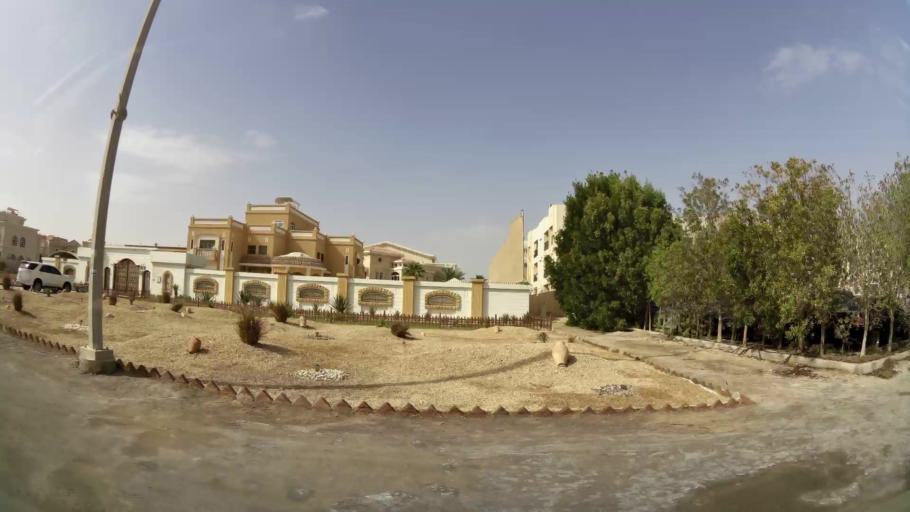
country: AE
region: Abu Dhabi
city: Abu Dhabi
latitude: 24.4233
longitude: 54.5608
